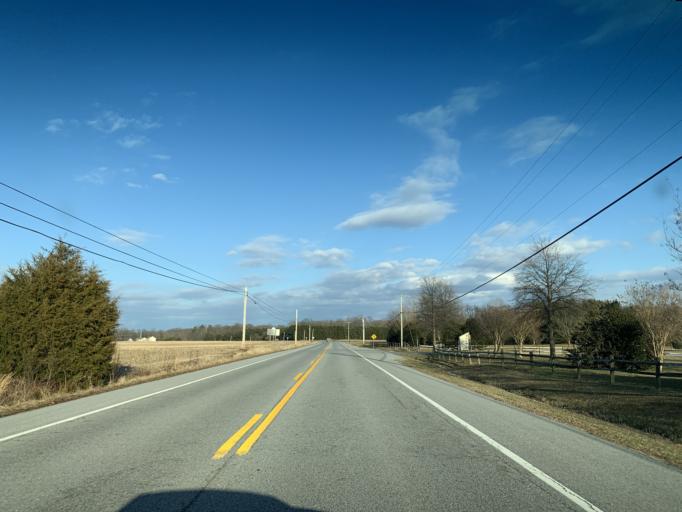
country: US
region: Maryland
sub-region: Queen Anne's County
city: Kingstown
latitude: 39.1488
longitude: -75.9745
